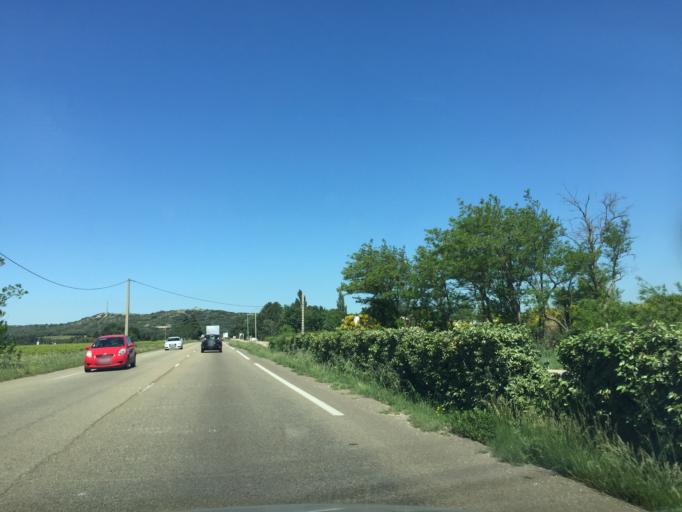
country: FR
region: Languedoc-Roussillon
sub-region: Departement du Gard
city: Saze
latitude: 43.9534
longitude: 4.6625
